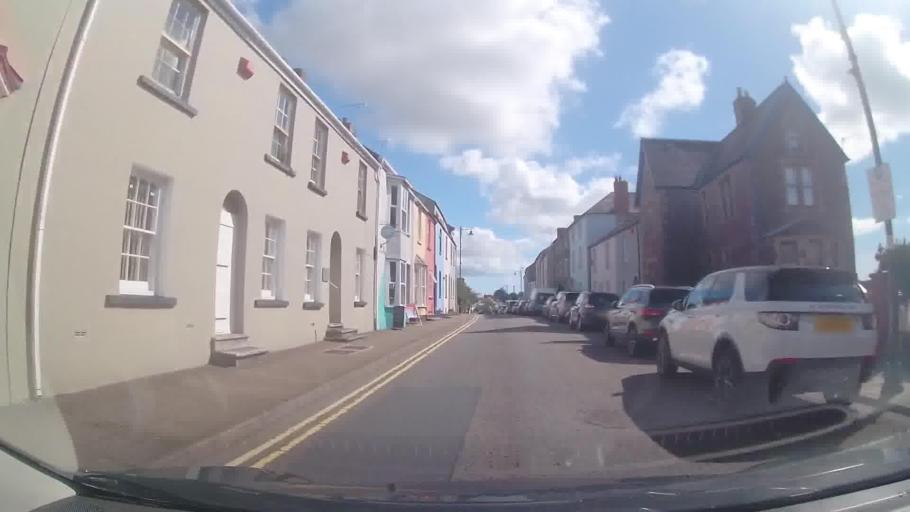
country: GB
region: Wales
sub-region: Pembrokeshire
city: Pembroke
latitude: 51.6747
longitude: -4.9127
